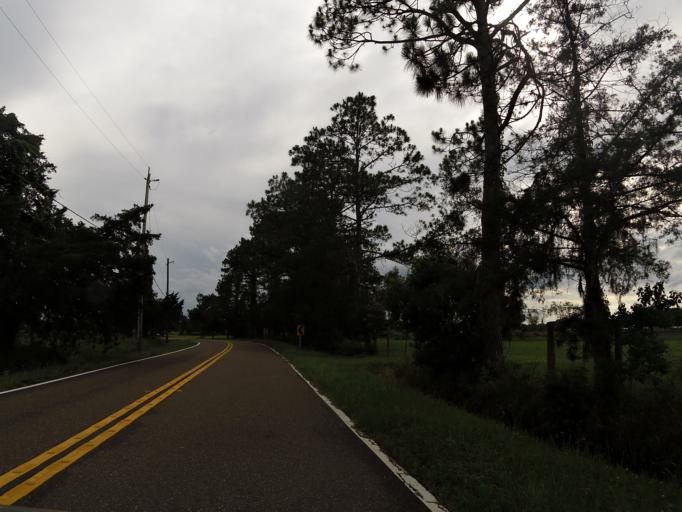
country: US
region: Florida
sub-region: Nassau County
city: Nassau Village-Ratliff
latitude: 30.5469
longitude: -81.7152
